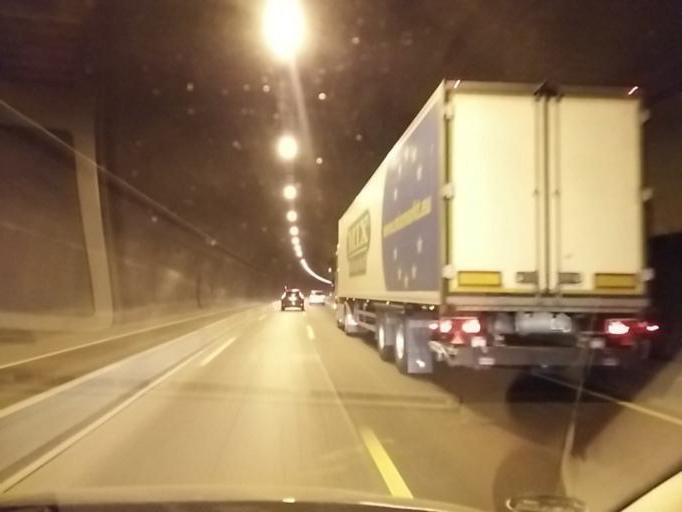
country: DE
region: Baden-Wuerttemberg
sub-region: Regierungsbezirk Stuttgart
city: Nufringen
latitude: 48.6036
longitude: 8.8964
